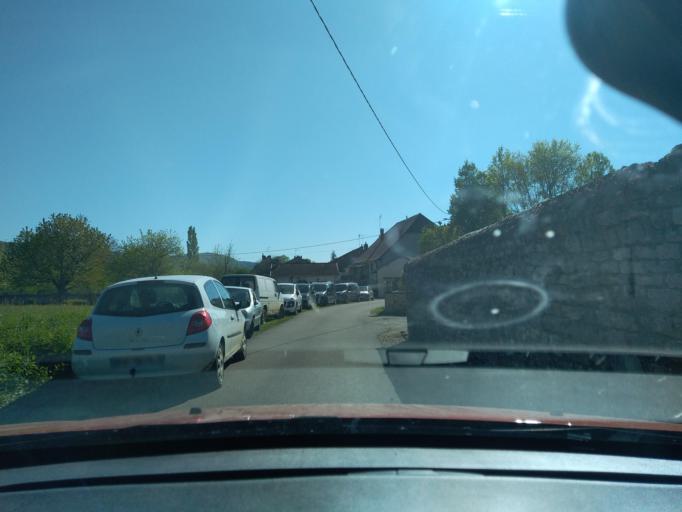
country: FR
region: Franche-Comte
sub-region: Departement du Jura
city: Montmorot
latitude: 46.6075
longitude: 5.4747
